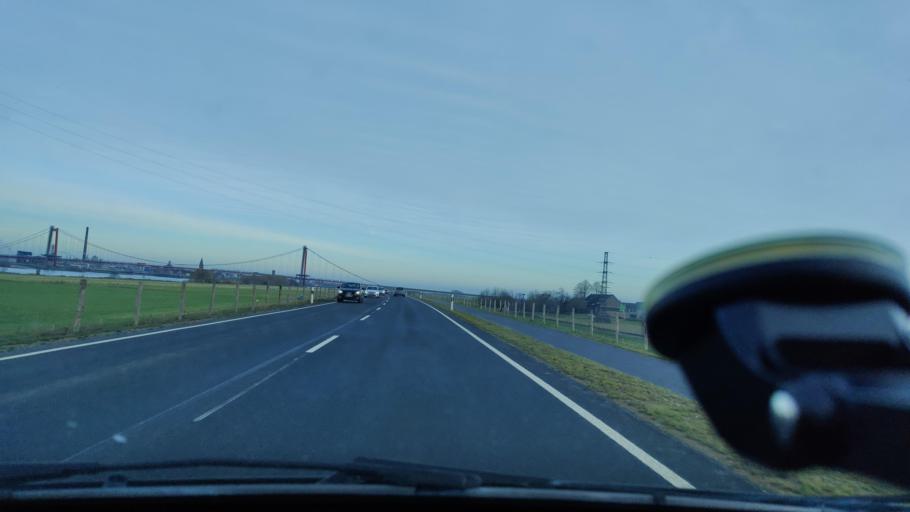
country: DE
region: North Rhine-Westphalia
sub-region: Regierungsbezirk Dusseldorf
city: Emmerich
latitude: 51.8247
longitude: 6.2063
